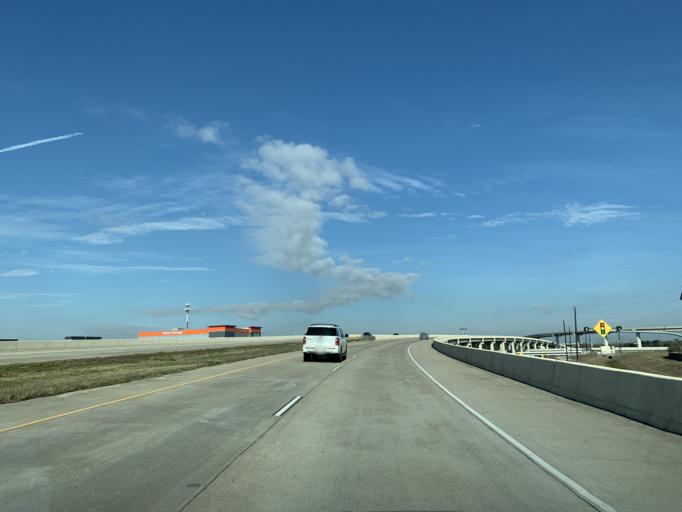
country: US
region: Texas
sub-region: Fort Bend County
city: Cinco Ranch
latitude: 29.6968
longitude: -95.7745
